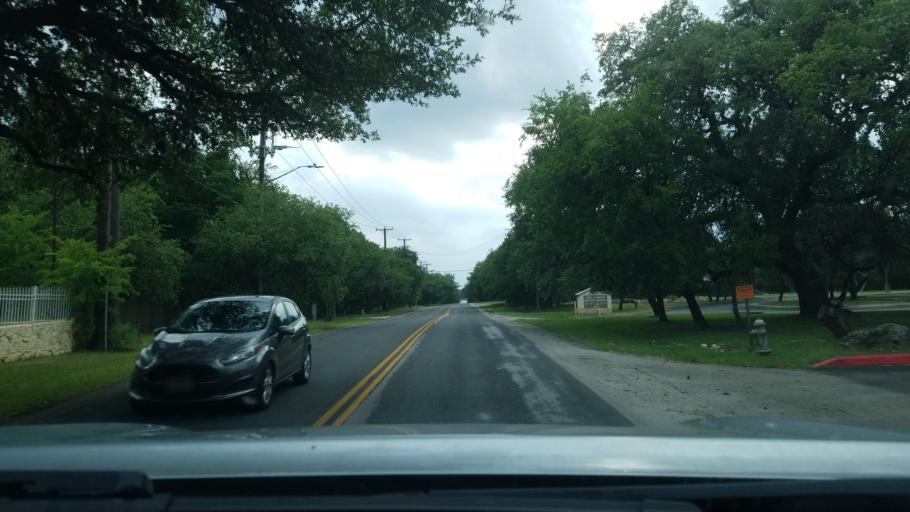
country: US
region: Texas
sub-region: Bexar County
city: Leon Valley
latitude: 29.5448
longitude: -98.5937
